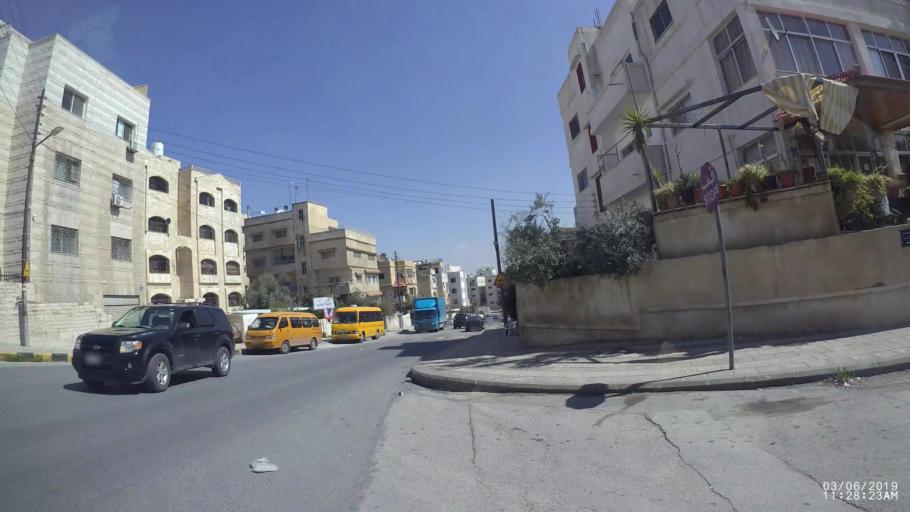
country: JO
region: Amman
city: Amman
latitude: 31.9806
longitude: 35.9917
